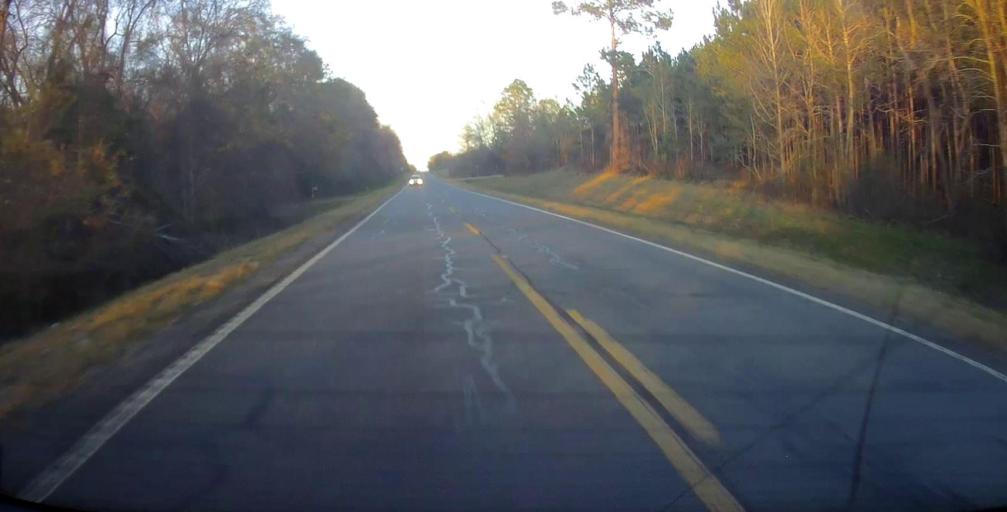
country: US
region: Georgia
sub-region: Dodge County
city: Eastman
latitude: 32.2738
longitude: -83.1170
